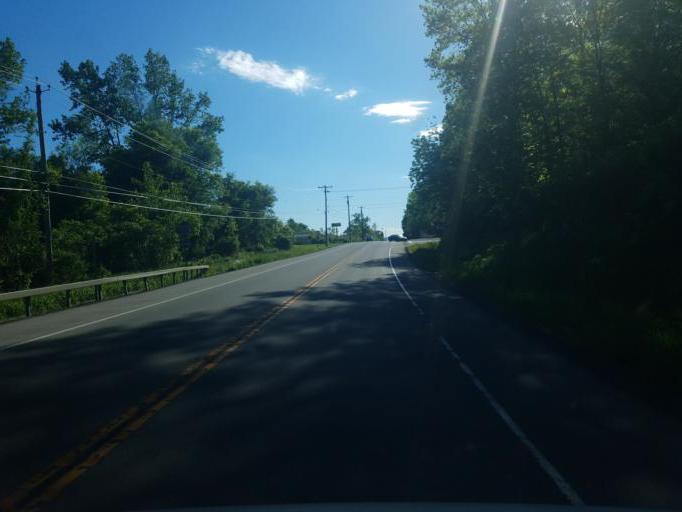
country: US
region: New York
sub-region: Herkimer County
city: Little Falls
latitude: 43.0234
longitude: -74.8931
